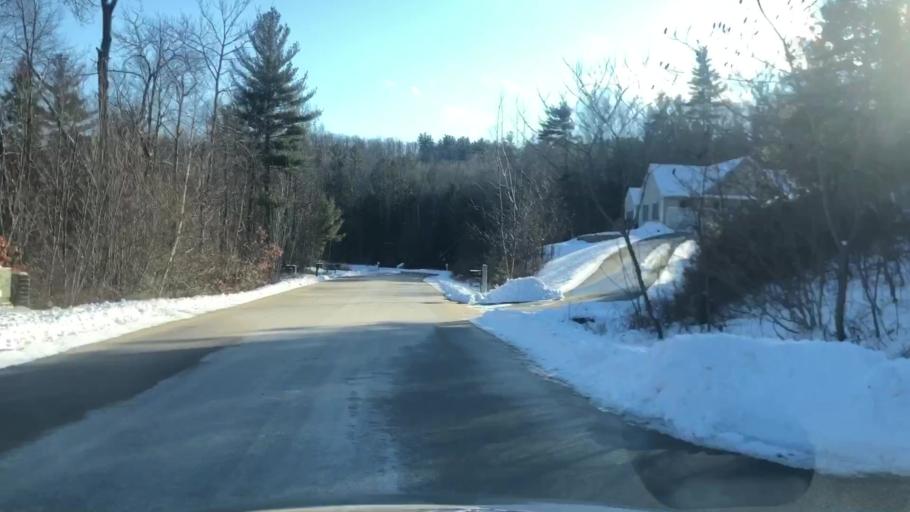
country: US
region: New Hampshire
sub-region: Hillsborough County
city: Wilton
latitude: 42.8111
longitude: -71.7152
